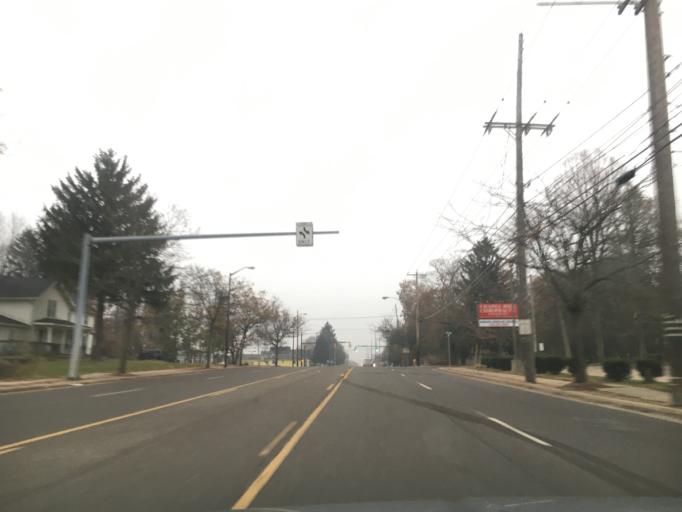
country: US
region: Ohio
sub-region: Summit County
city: Cuyahoga Falls
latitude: 41.1126
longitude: -81.4861
